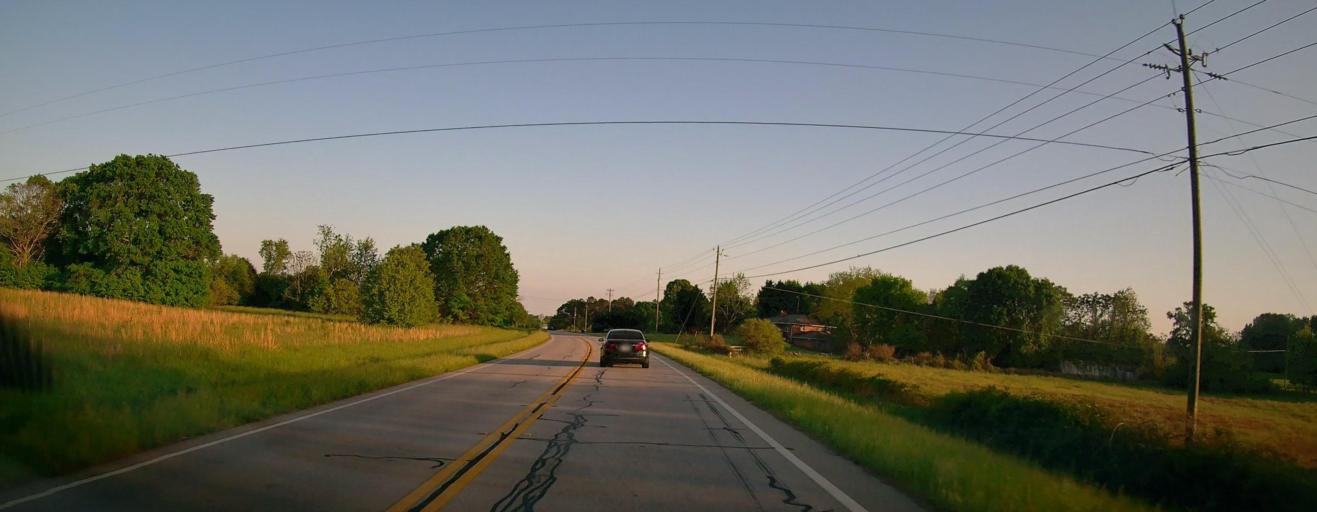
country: US
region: Georgia
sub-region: Newton County
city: Oakwood
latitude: 33.5266
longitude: -83.9522
